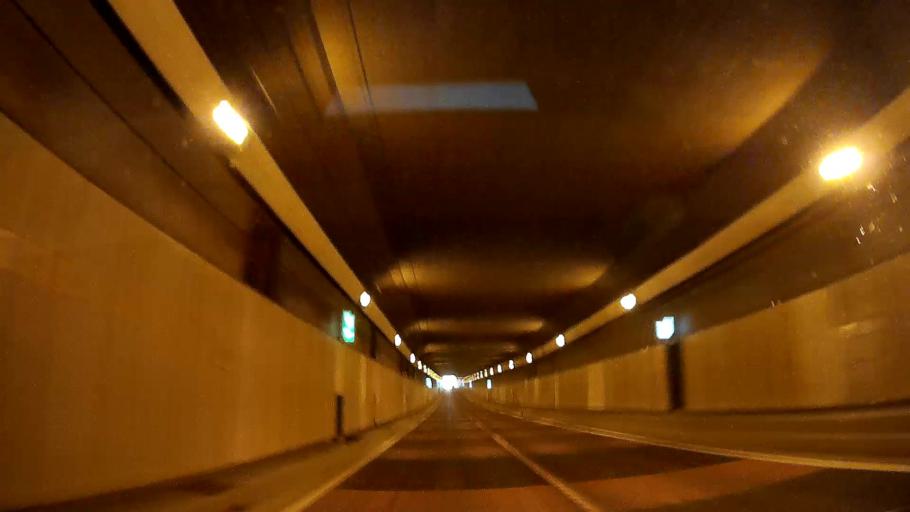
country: JP
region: Kanagawa
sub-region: Kawasaki-shi
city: Kawasaki
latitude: 35.6035
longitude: 139.7932
